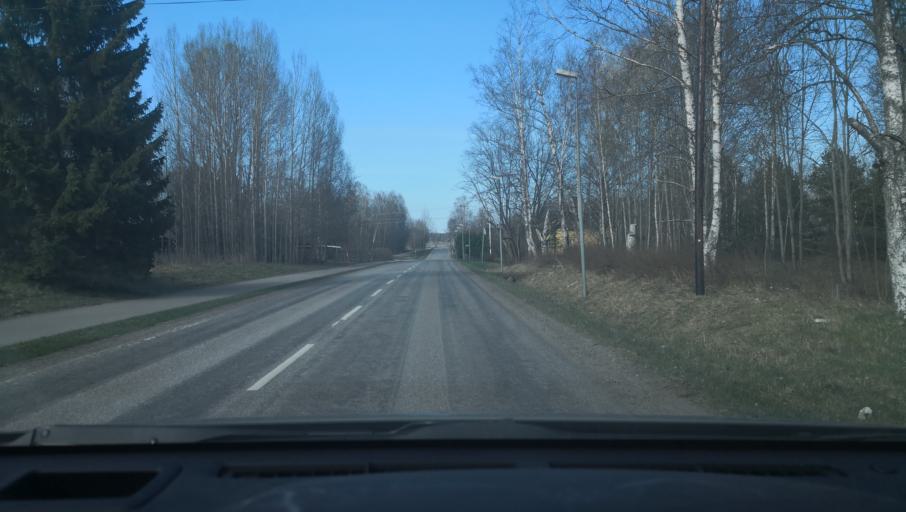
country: SE
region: Uppsala
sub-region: Heby Kommun
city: Heby
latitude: 59.9428
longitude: 16.8640
